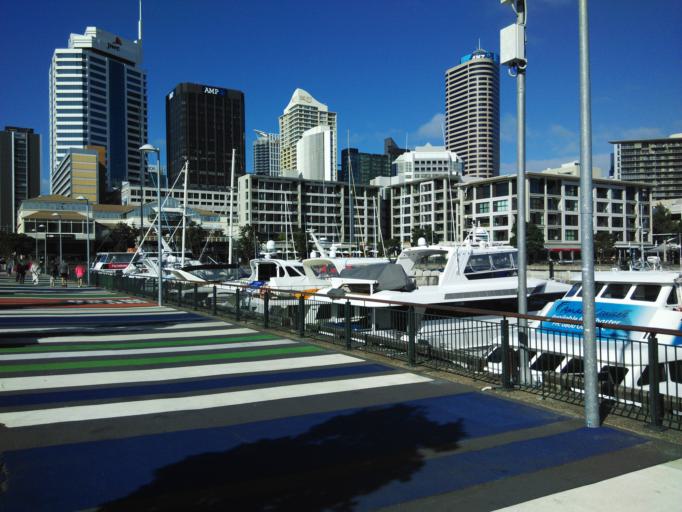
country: NZ
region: Auckland
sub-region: Auckland
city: Auckland
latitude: -36.8421
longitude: 174.7620
